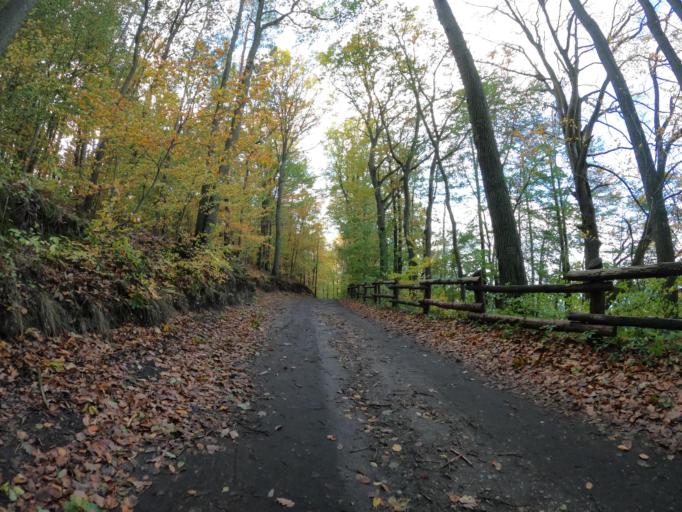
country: PL
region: West Pomeranian Voivodeship
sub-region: Powiat mysliborski
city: Barlinek
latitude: 52.9822
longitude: 15.2286
